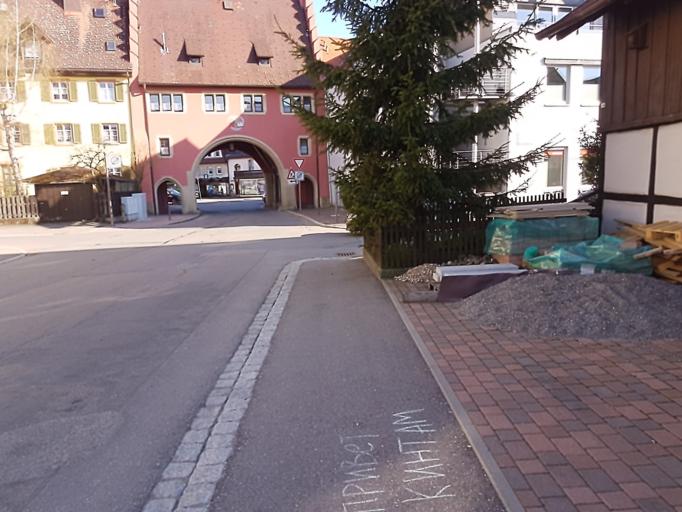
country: DE
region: Baden-Wuerttemberg
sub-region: Freiburg Region
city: Loffingen
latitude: 47.8843
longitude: 8.3434
